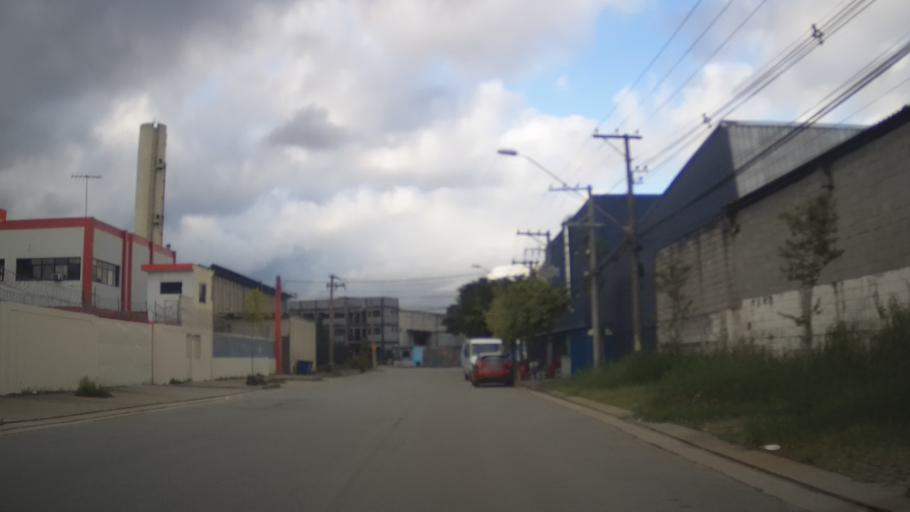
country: BR
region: Sao Paulo
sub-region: Guarulhos
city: Guarulhos
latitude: -23.4752
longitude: -46.4653
